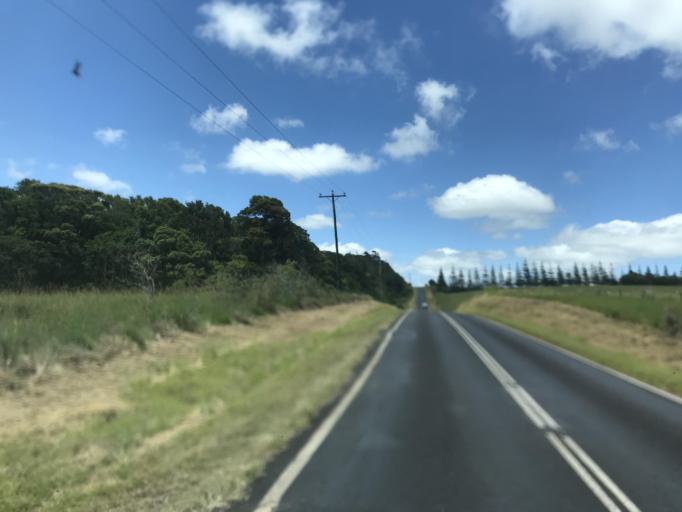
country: AU
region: Queensland
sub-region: Tablelands
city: Ravenshoe
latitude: -17.5028
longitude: 145.4764
